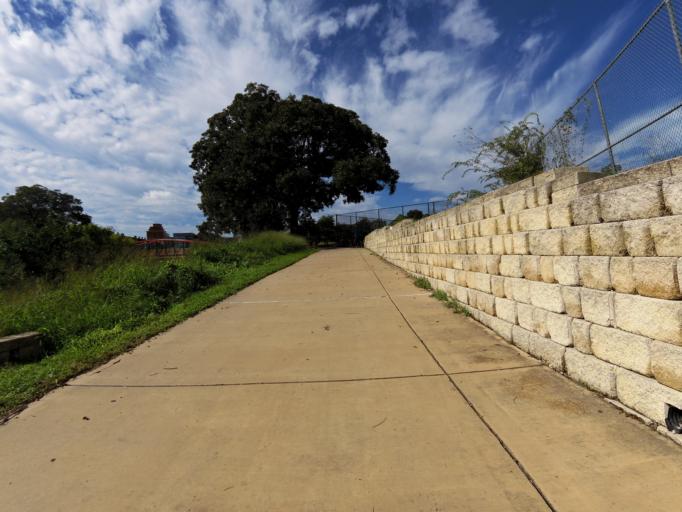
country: US
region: Texas
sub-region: Bexar County
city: San Antonio
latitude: 29.4042
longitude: -98.4896
